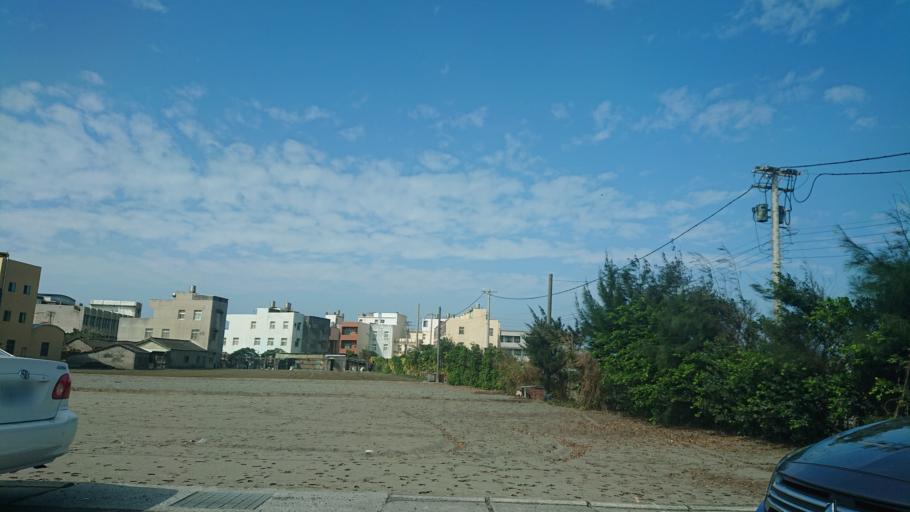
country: TW
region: Taiwan
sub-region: Changhua
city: Chang-hua
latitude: 23.9237
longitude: 120.3223
